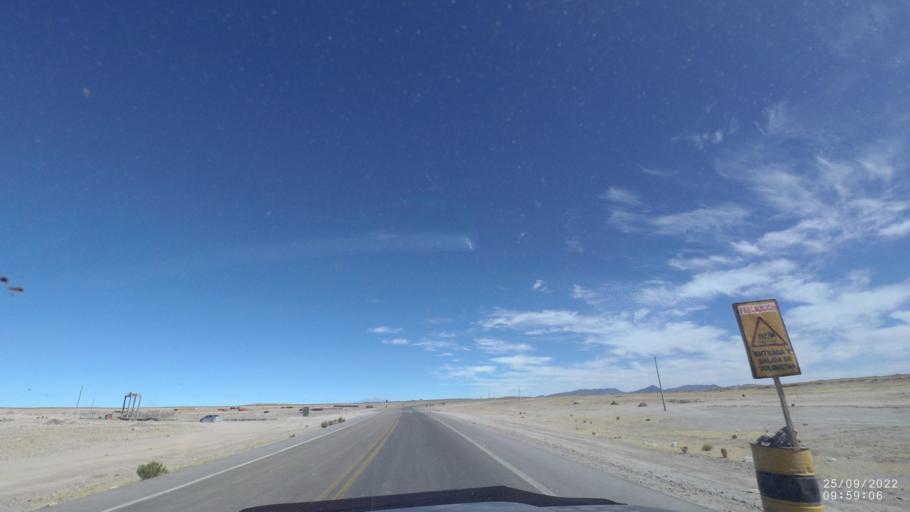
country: BO
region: Potosi
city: Colchani
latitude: -20.2968
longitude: -66.9351
